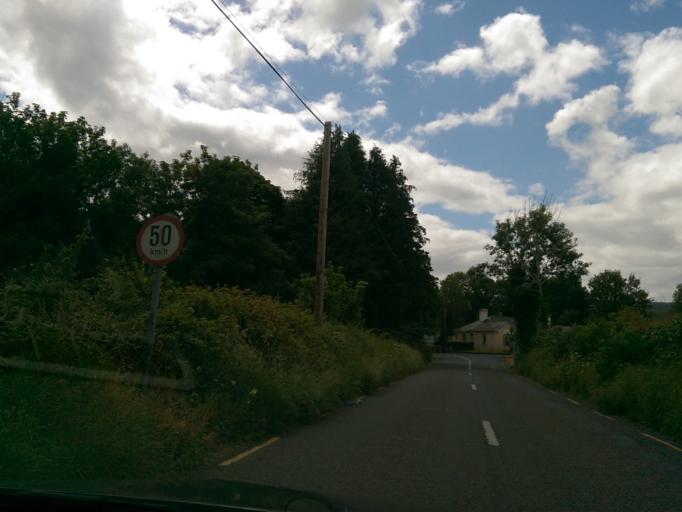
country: IE
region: Munster
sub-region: North Tipperary
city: Nenagh
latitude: 52.7982
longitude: -8.1914
